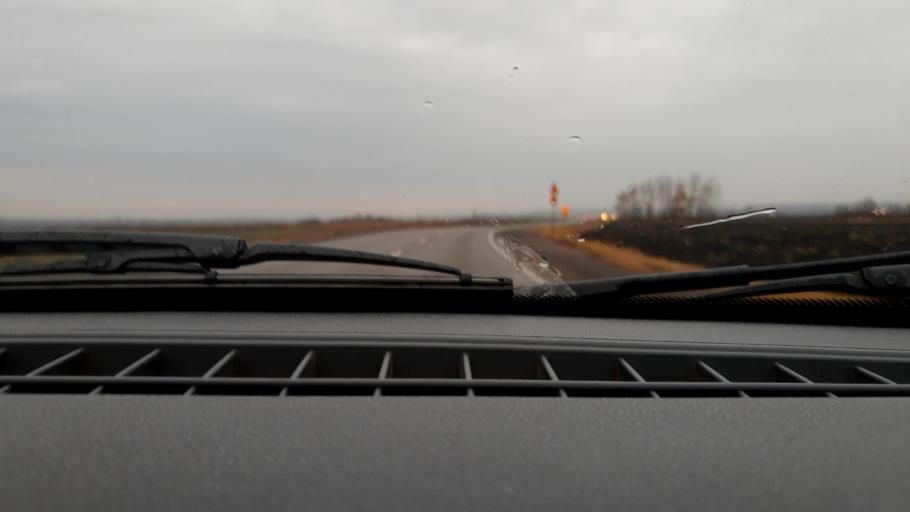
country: RU
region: Bashkortostan
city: Ufa
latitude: 54.8035
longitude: 55.9637
